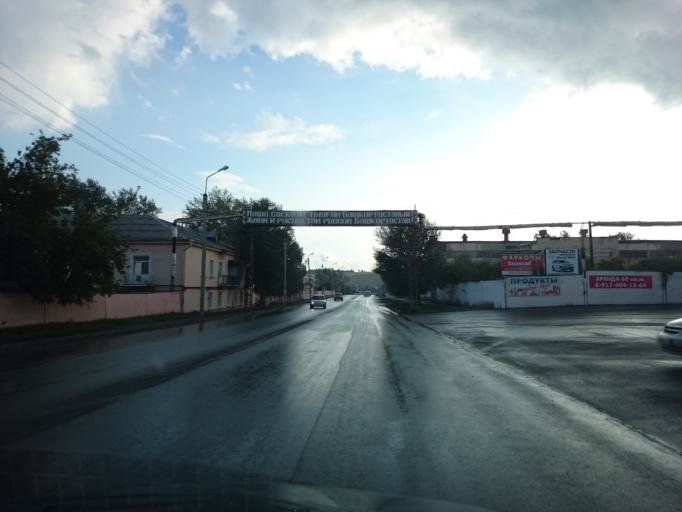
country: RU
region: Bashkortostan
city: Beloretsk
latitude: 53.9579
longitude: 58.3623
